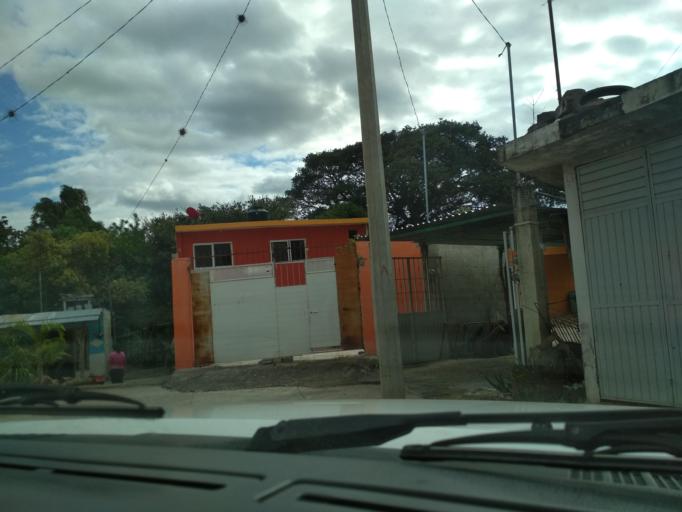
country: MX
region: Veracruz
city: Alto Lucero
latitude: 19.5900
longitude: -96.7821
